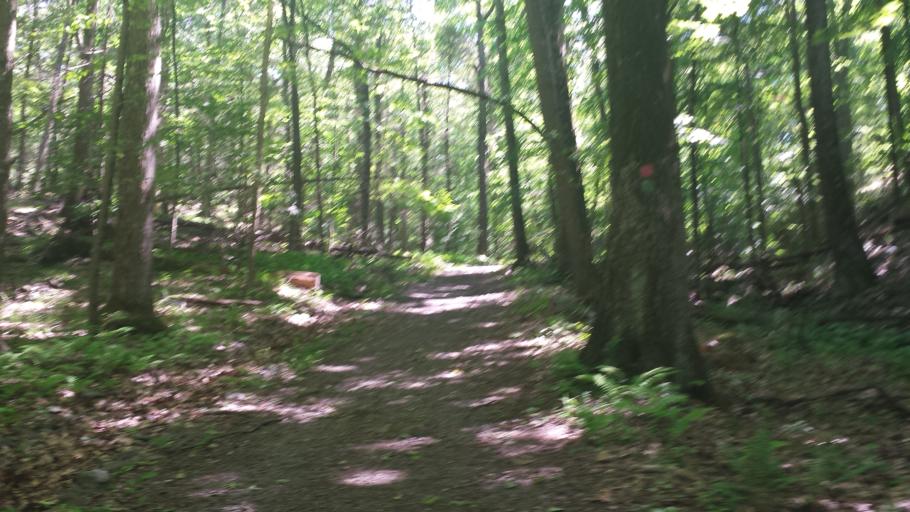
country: US
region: New York
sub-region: Westchester County
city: Pound Ridge
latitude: 41.2351
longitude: -73.5940
